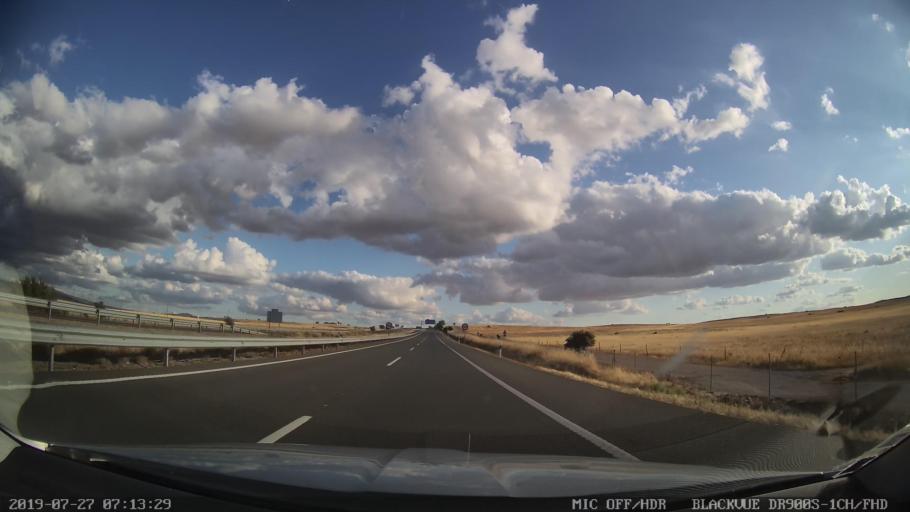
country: ES
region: Extremadura
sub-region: Provincia de Caceres
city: Trujillo
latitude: 39.5109
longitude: -5.8369
